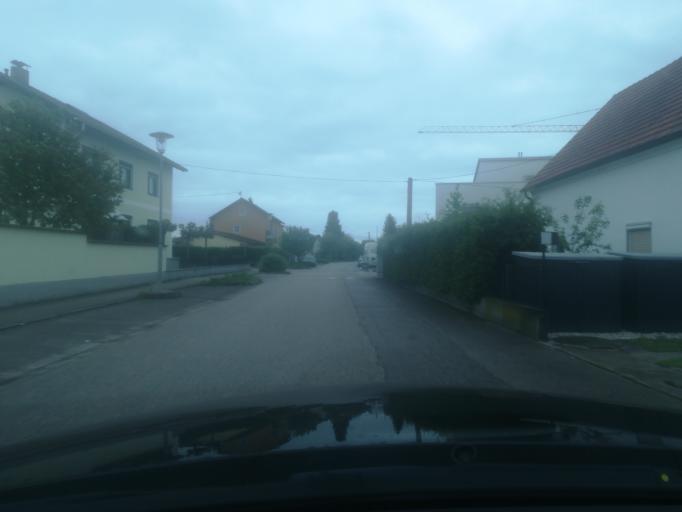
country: AT
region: Upper Austria
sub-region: Wels-Land
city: Marchtrenk
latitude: 48.1946
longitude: 14.1205
